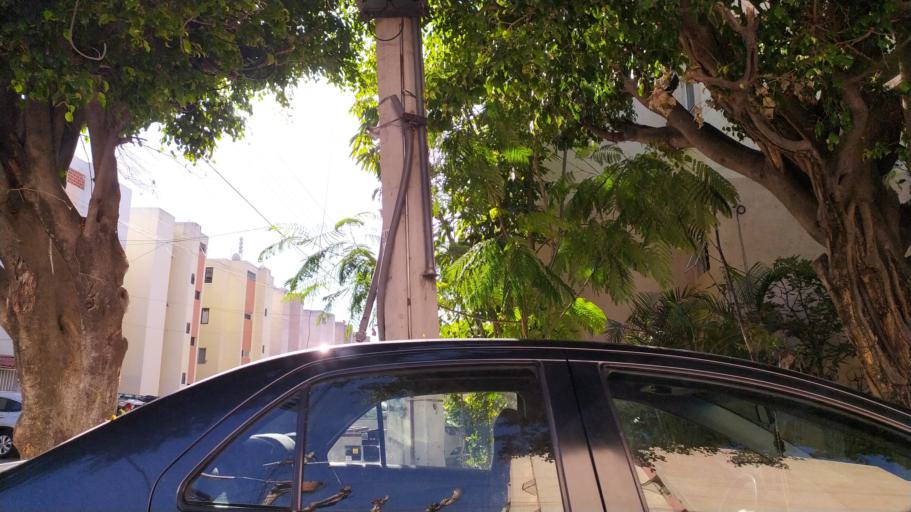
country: MX
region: Jalisco
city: Guadalajara
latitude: 20.6549
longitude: -103.4307
